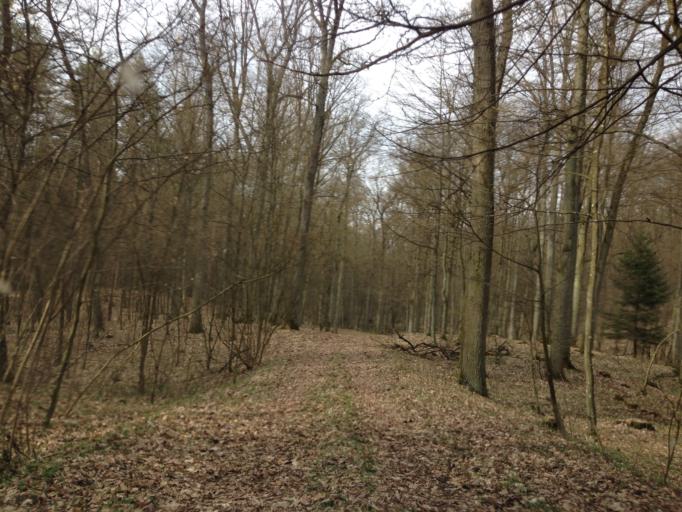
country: PL
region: Kujawsko-Pomorskie
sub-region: Powiat brodnicki
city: Gorzno
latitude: 53.2265
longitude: 19.7299
